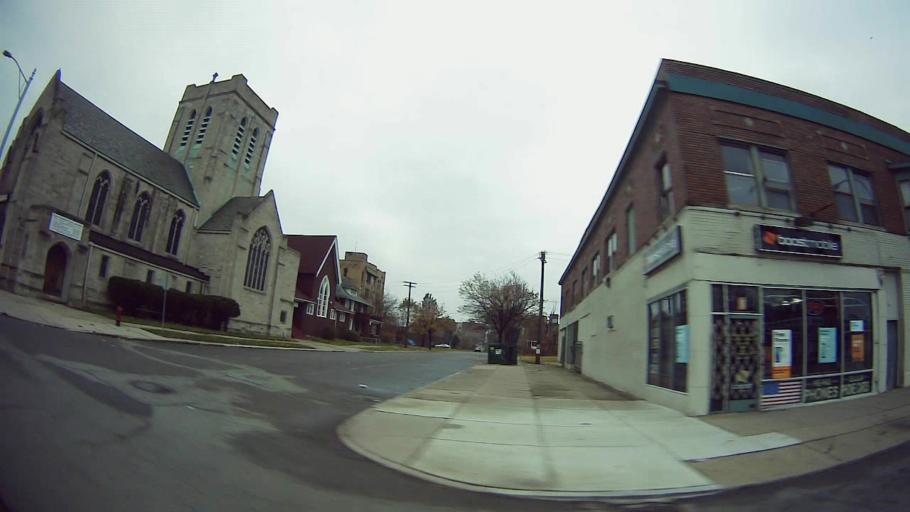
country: US
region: Michigan
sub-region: Wayne County
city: Highland Park
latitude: 42.3981
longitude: -83.0921
